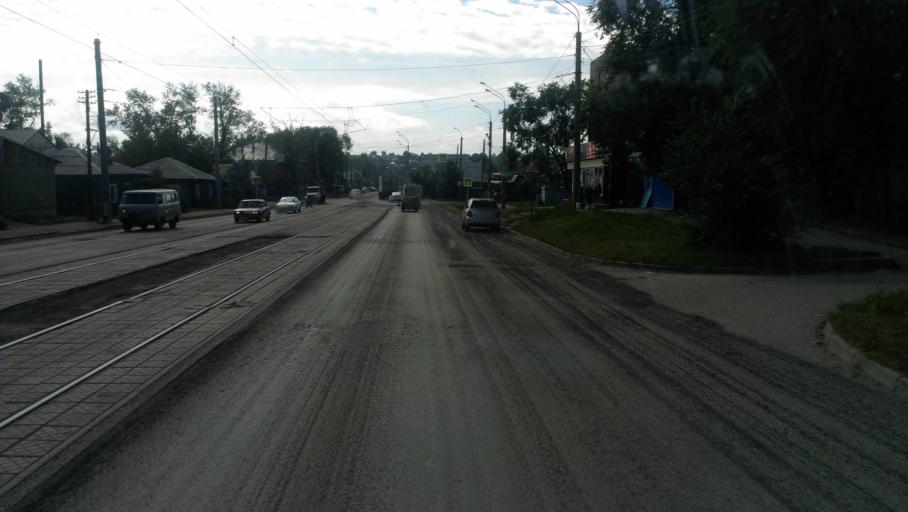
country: RU
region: Altai Krai
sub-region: Gorod Barnaulskiy
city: Barnaul
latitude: 53.3279
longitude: 83.7624
